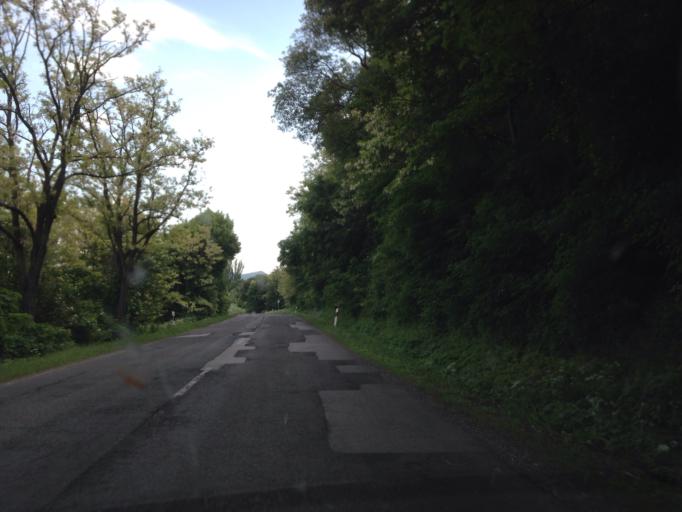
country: HU
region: Pest
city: Szob
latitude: 47.8094
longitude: 18.8390
